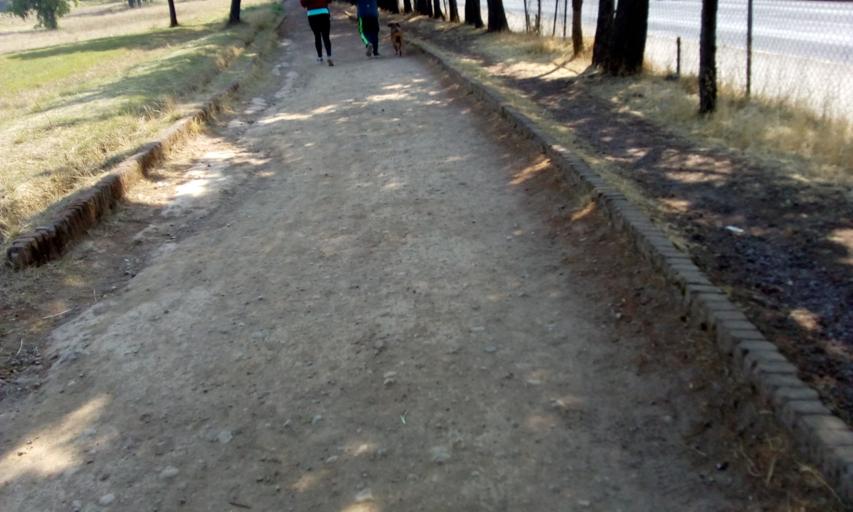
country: MX
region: Mexico
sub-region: Toluca
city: San Antonio Buenavista
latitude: 19.2716
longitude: -99.6955
